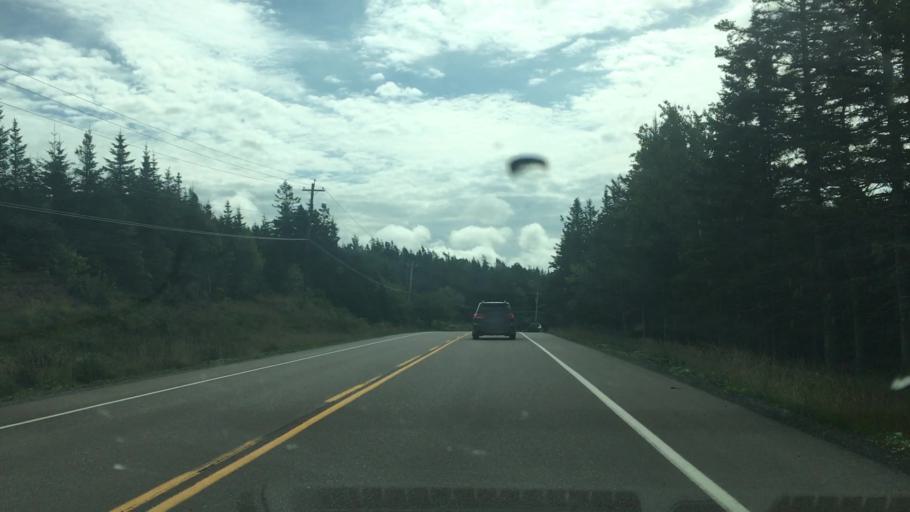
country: CA
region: Nova Scotia
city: Princeville
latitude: 45.7029
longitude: -60.7392
